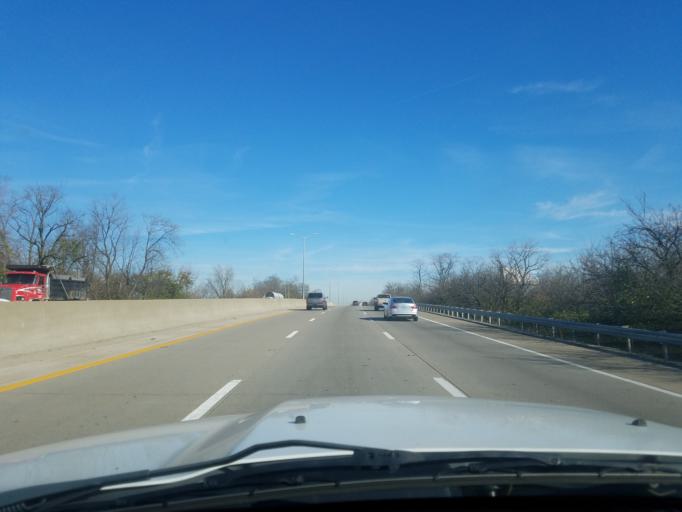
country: US
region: Kentucky
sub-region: Jefferson County
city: Shively
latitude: 38.2314
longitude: -85.8209
